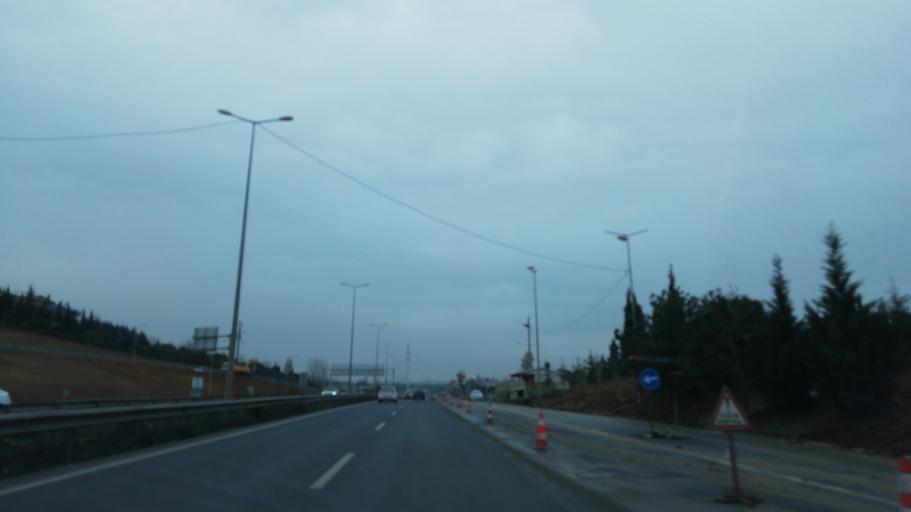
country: TR
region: Kocaeli
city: Darica
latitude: 40.8139
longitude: 29.3654
